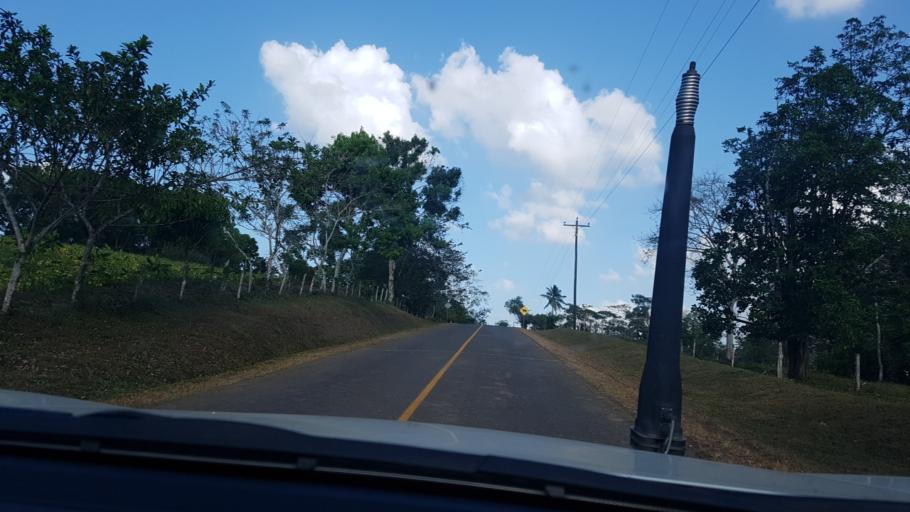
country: NI
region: Atlantico Sur
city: Nueva Guinea
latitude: 11.6954
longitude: -84.4117
